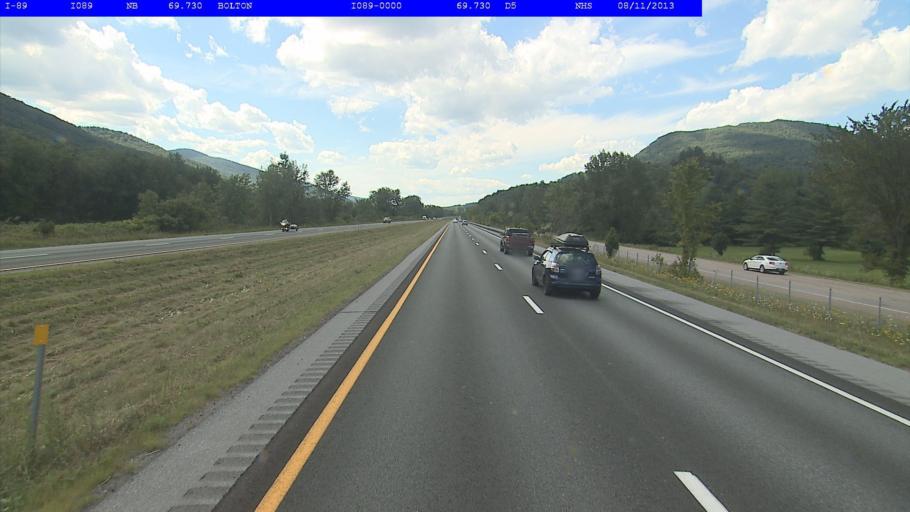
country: US
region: Vermont
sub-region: Washington County
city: Waterbury
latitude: 44.3686
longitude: -72.8631
